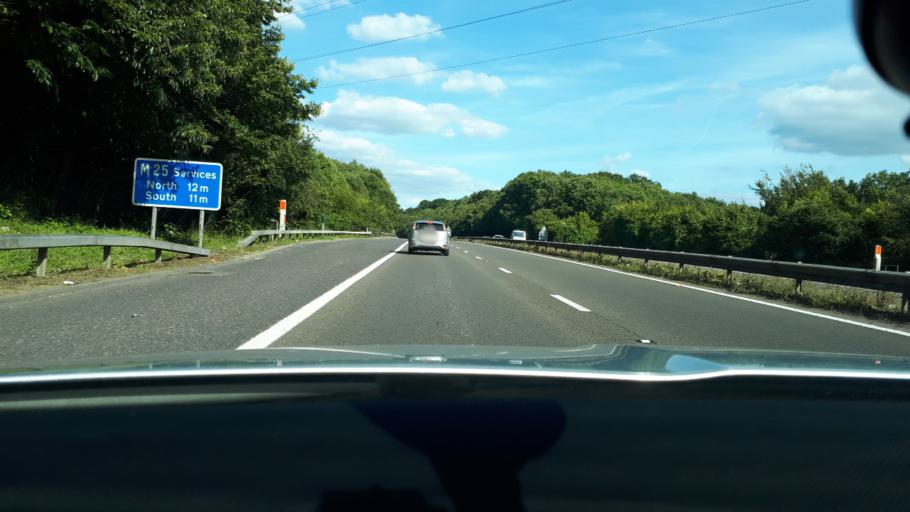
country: GB
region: England
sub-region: Kent
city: Halstead
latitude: 51.3465
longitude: 0.1421
